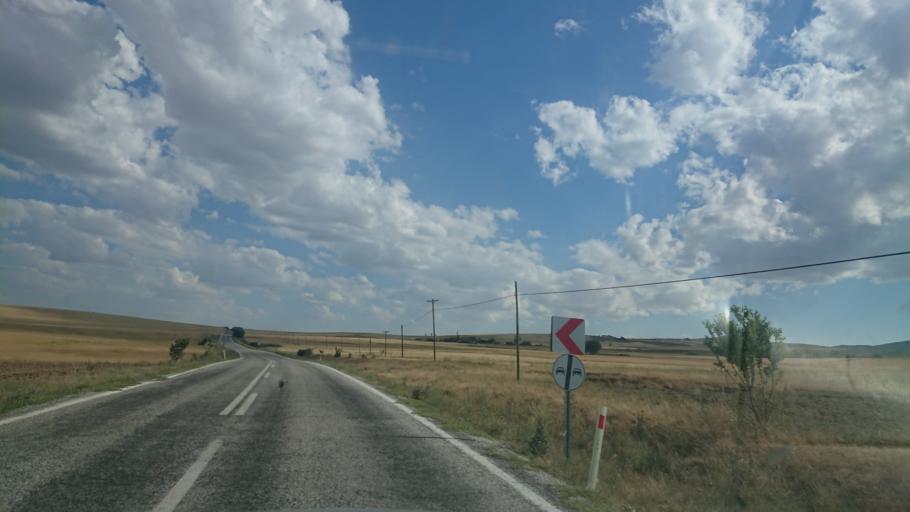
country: TR
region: Aksaray
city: Sariyahsi
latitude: 38.9367
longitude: 33.8327
